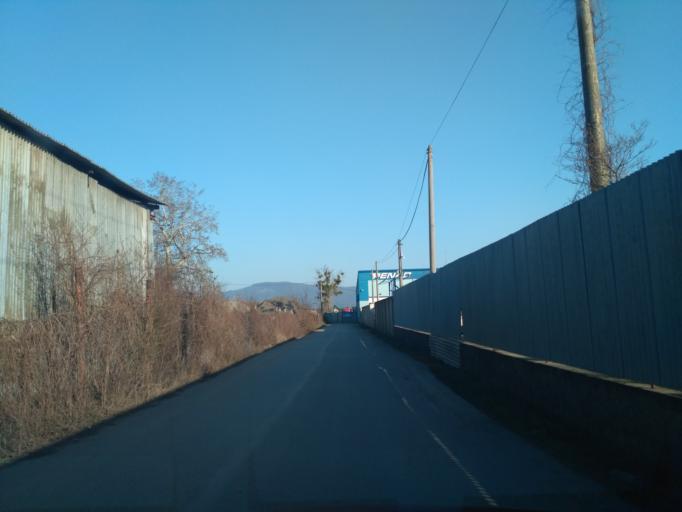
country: SK
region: Kosicky
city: Kosice
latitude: 48.6696
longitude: 21.2977
